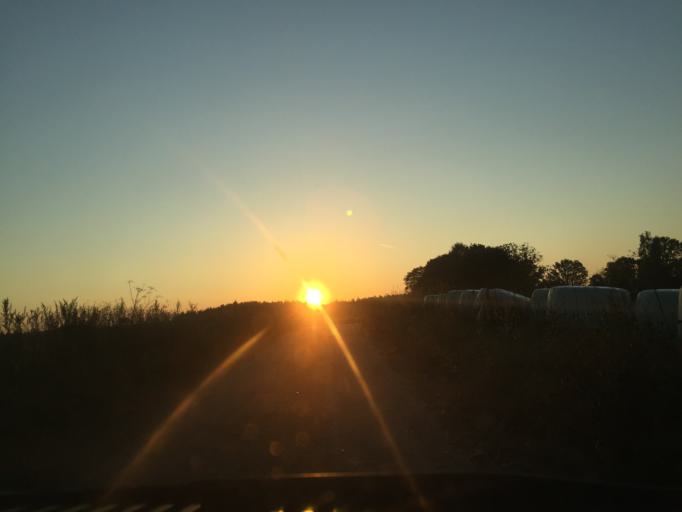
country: LV
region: Vecpiebalga
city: Vecpiebalga
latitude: 57.0636
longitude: 25.7545
